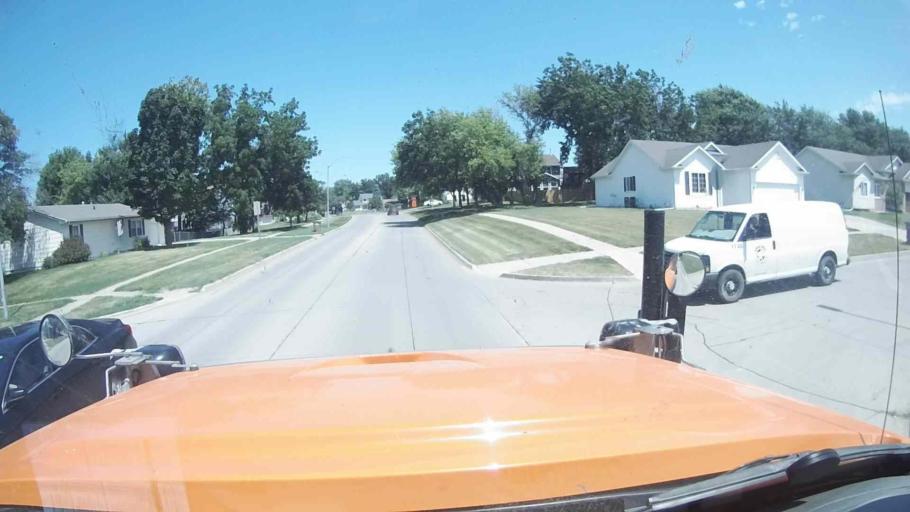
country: US
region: Iowa
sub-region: Polk County
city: Altoona
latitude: 41.6543
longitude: -93.4693
